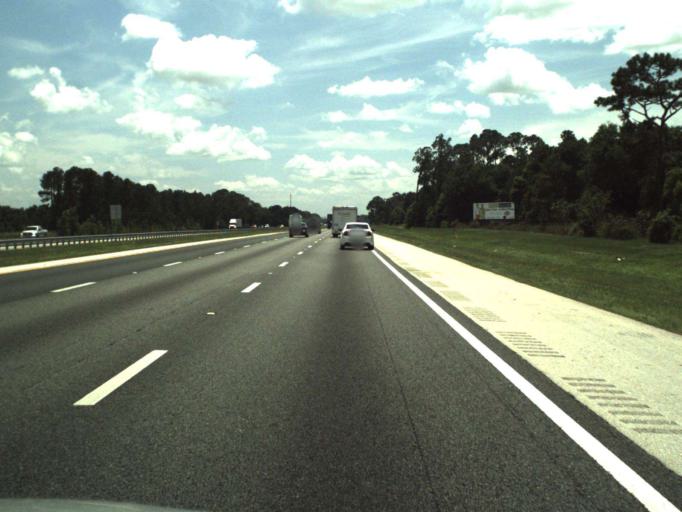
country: US
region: Florida
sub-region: Volusia County
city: Lake Helen
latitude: 28.9958
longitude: -81.2450
